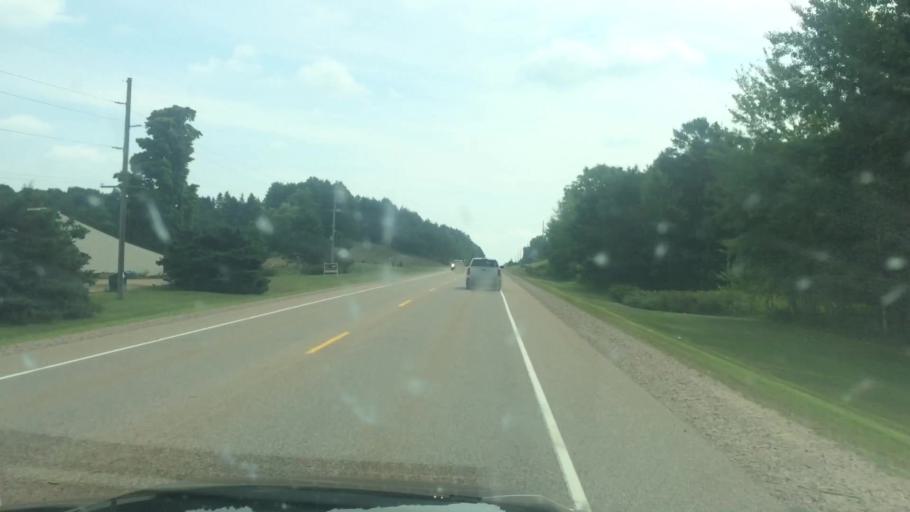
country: US
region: Wisconsin
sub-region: Langlade County
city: Antigo
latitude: 45.1618
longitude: -89.0648
